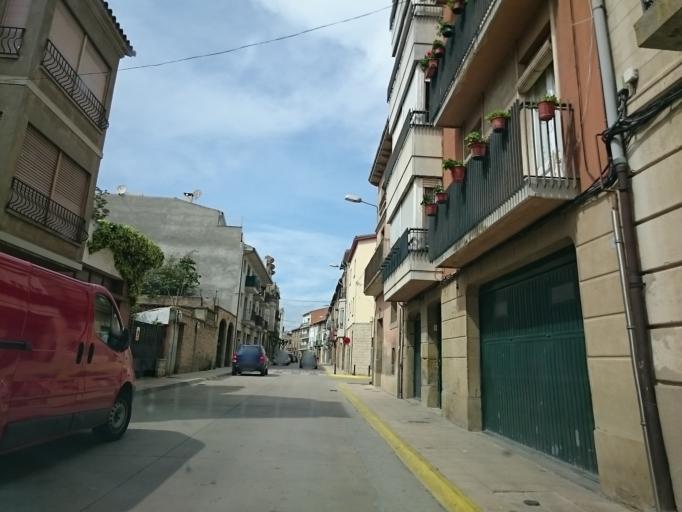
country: ES
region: Catalonia
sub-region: Provincia de Lleida
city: Ivorra
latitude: 41.7852
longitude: 1.2899
